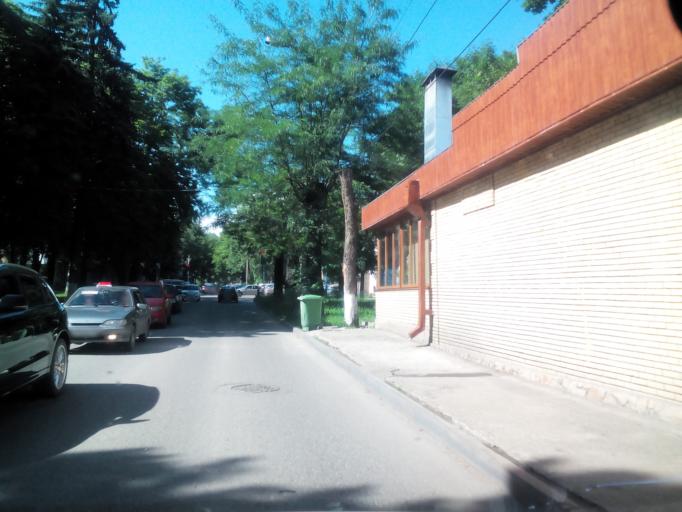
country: RU
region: Stavropol'skiy
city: Pyatigorsk
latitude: 44.0360
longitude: 43.0621
